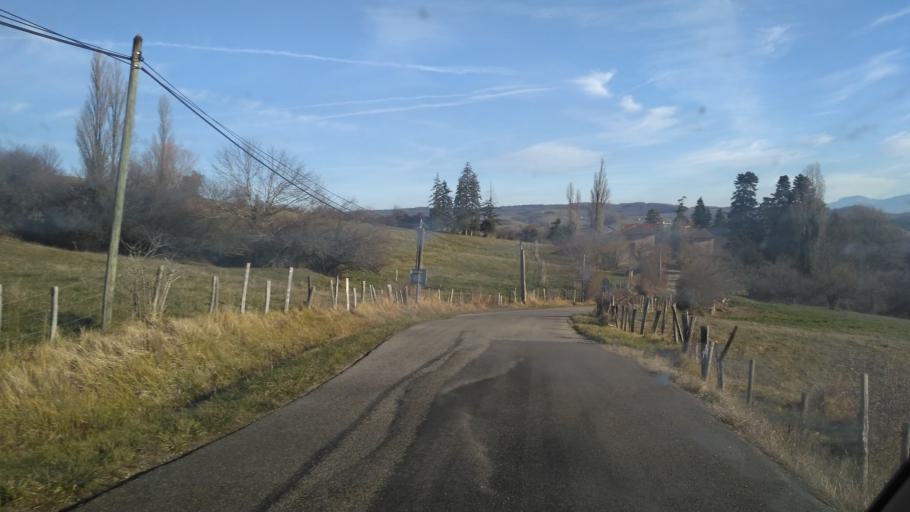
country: FR
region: Rhone-Alpes
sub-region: Departement de l'Isere
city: Saint-Antoine-l'Abbaye
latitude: 45.1749
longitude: 5.2006
